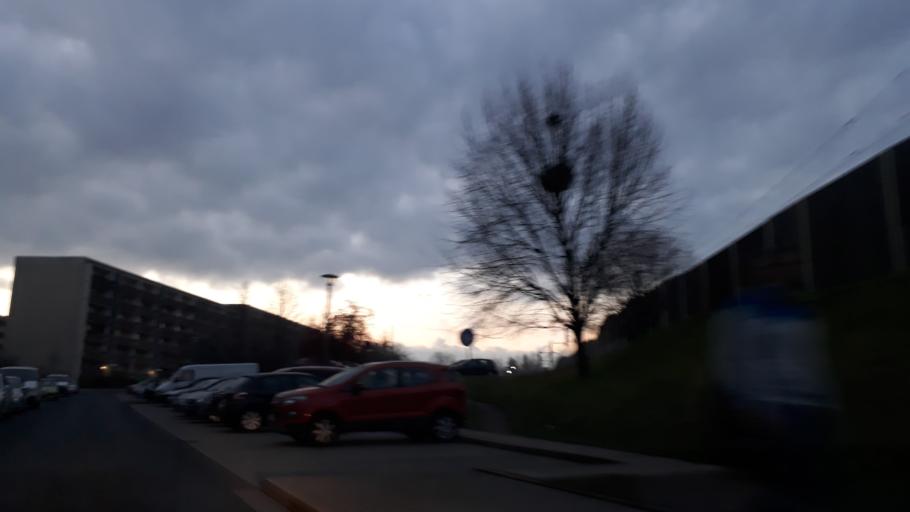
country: DE
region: Saxony
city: Freital
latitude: 51.0480
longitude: 13.6632
